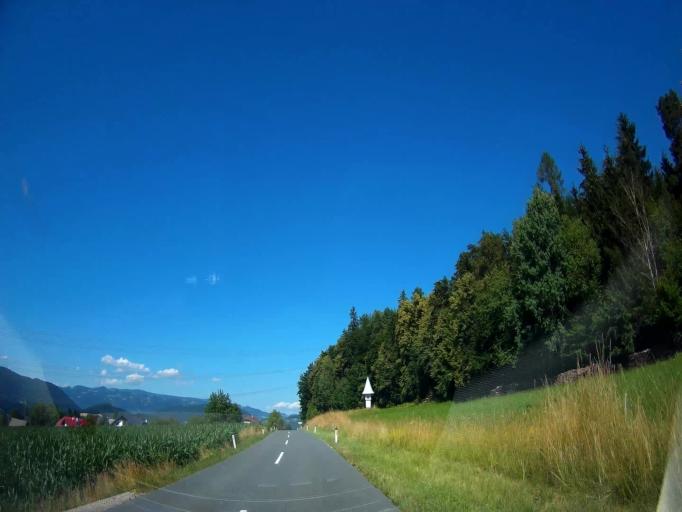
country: AT
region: Carinthia
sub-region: Politischer Bezirk Volkermarkt
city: Gallizien
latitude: 46.6142
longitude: 14.5531
